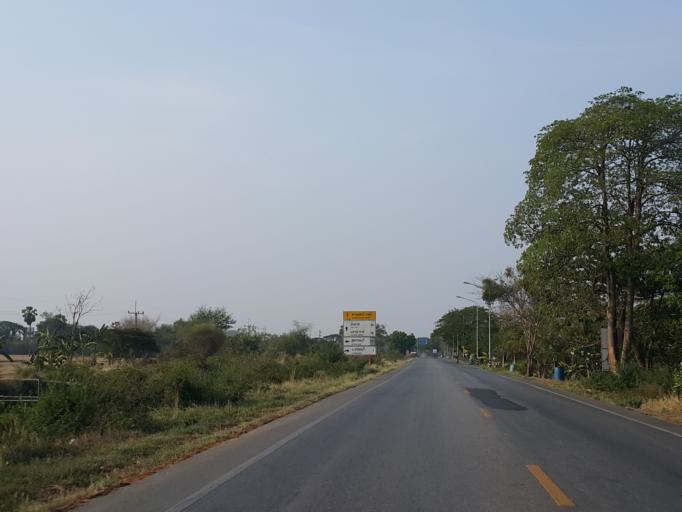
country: TH
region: Chai Nat
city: Sankhaburi
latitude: 15.0375
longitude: 100.1462
